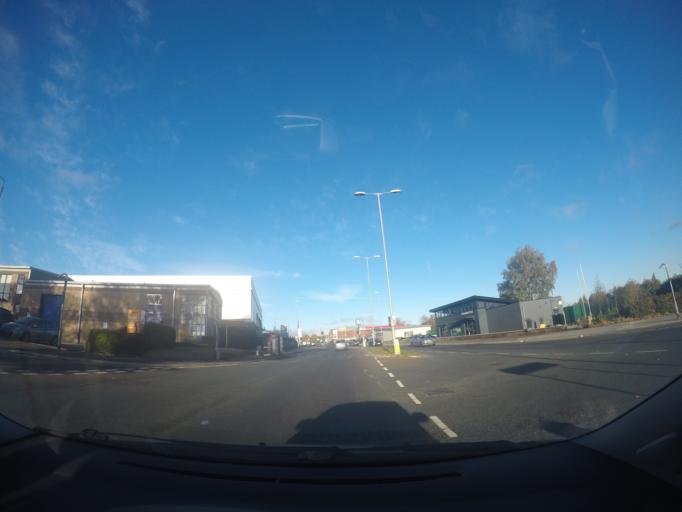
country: GB
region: England
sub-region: City and Borough of Leeds
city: Leeds
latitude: 53.7975
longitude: -1.5752
